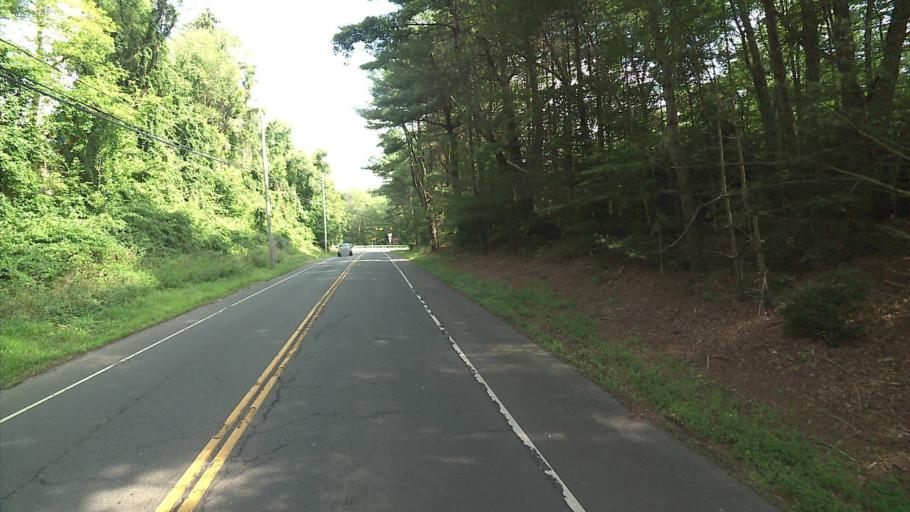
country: US
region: Connecticut
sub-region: Middlesex County
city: Chester Center
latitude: 41.3582
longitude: -72.4996
